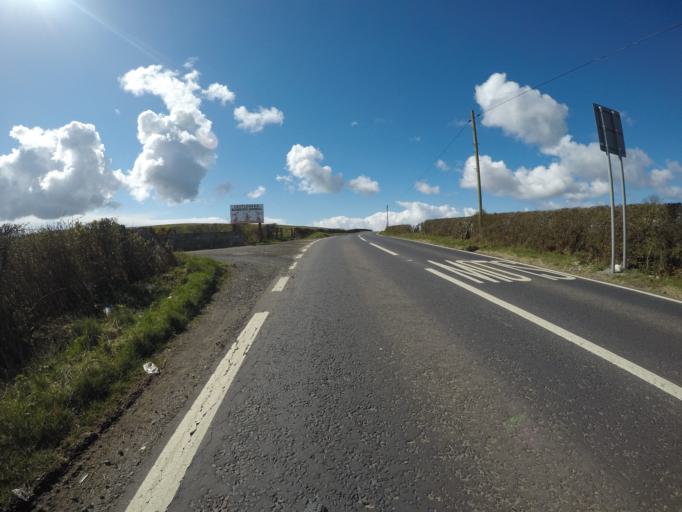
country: GB
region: Scotland
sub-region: North Ayrshire
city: Dalry
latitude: 55.6982
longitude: -4.7308
